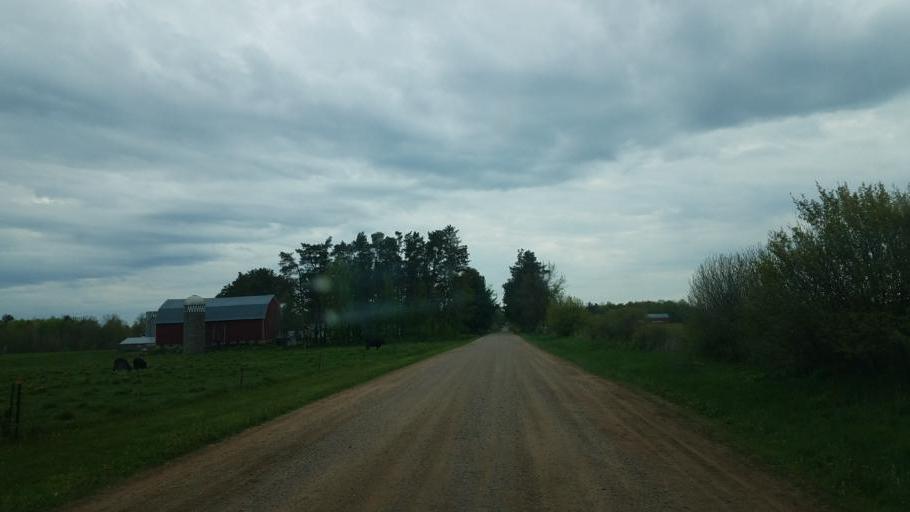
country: US
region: Wisconsin
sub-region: Marathon County
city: Spencer
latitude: 44.6049
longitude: -90.3766
